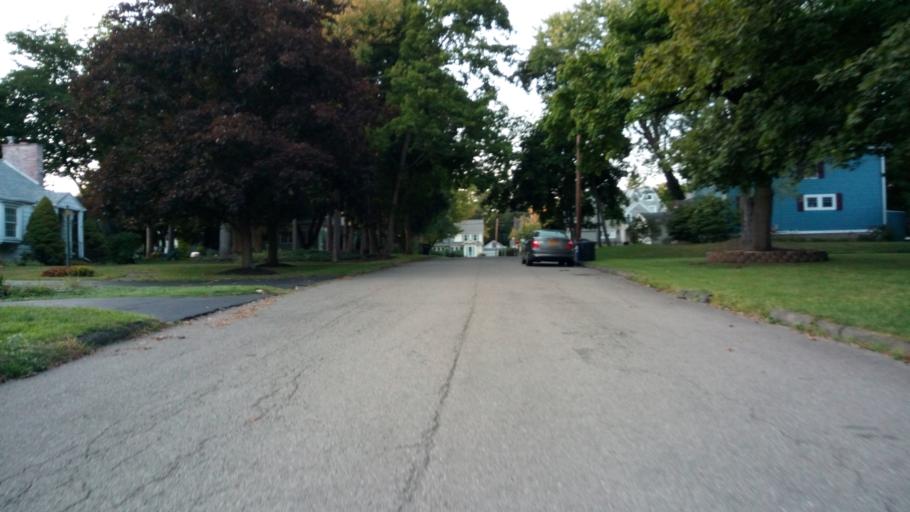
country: US
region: New York
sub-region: Chemung County
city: West Elmira
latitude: 42.0773
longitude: -76.8384
